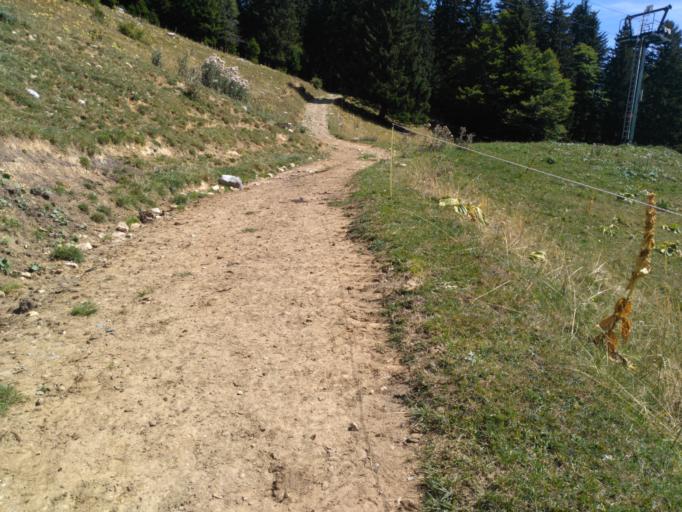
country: FR
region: Rhone-Alpes
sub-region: Departement de la Haute-Savoie
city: Gruffy
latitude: 45.7845
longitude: 6.1073
